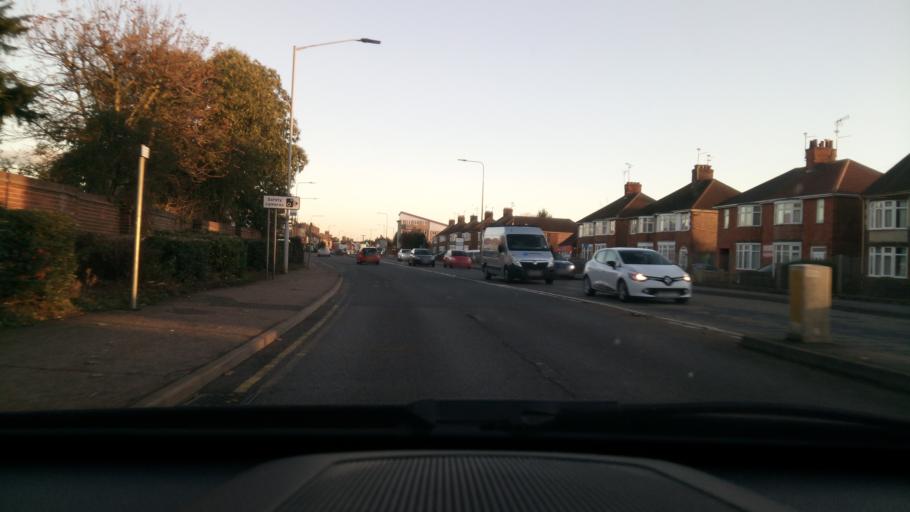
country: GB
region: England
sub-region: Peterborough
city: Peterborough
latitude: 52.6033
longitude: -0.2691
